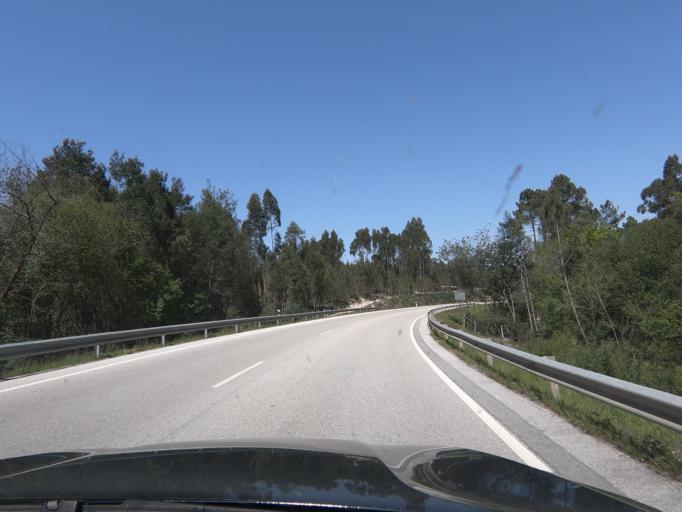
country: PT
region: Coimbra
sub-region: Lousa
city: Lousa
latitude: 40.1196
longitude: -8.2855
